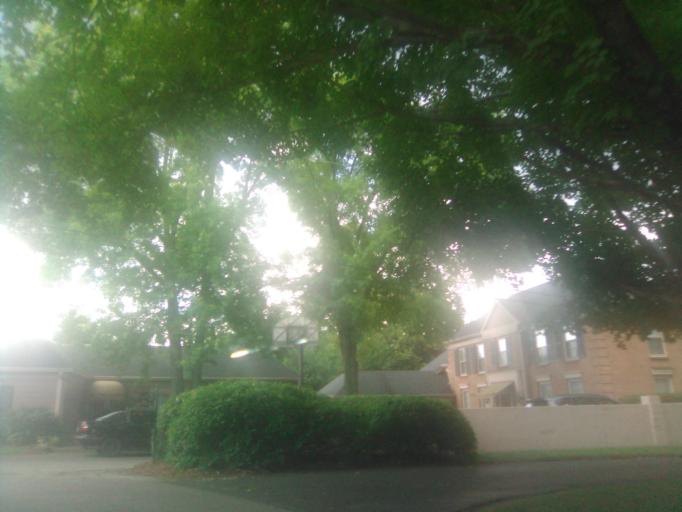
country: US
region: Tennessee
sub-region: Davidson County
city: Belle Meade
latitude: 36.1079
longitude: -86.8321
